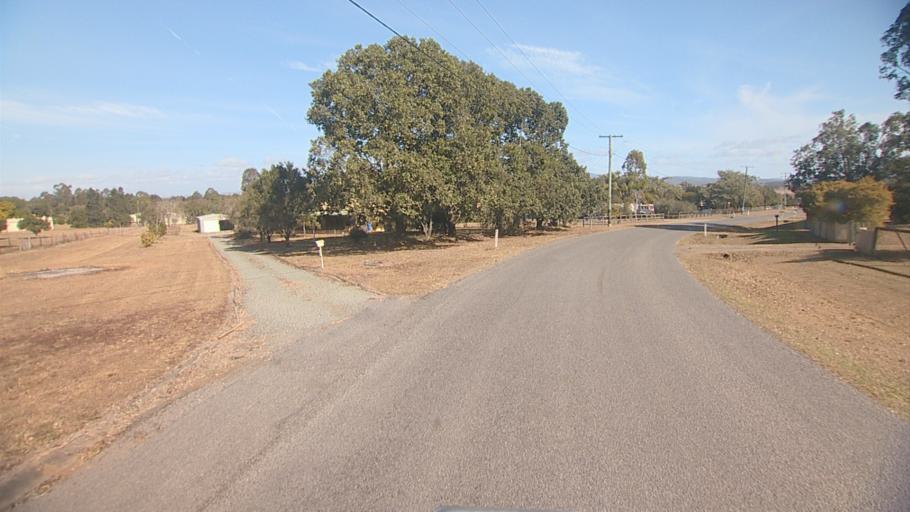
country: AU
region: Queensland
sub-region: Logan
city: Cedar Vale
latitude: -27.8658
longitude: 152.9712
